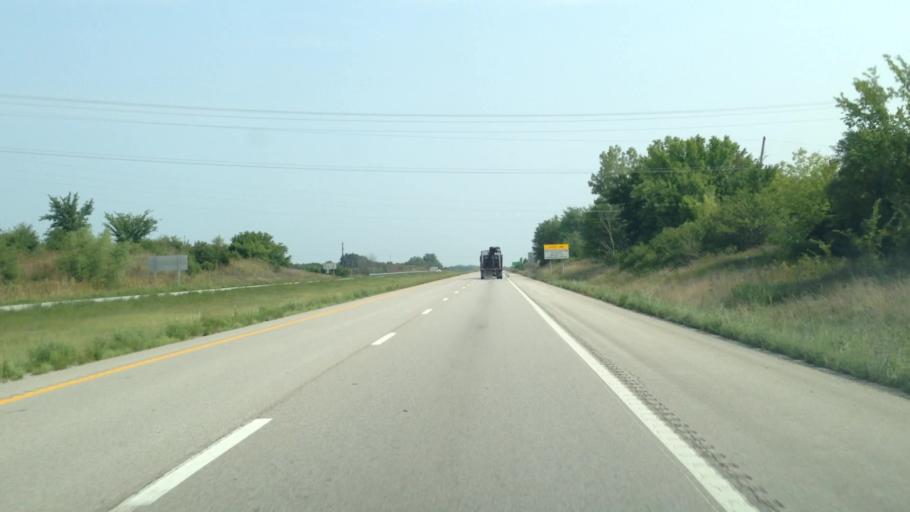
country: US
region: Missouri
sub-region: Clinton County
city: Cameron
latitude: 39.7602
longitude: -94.2180
